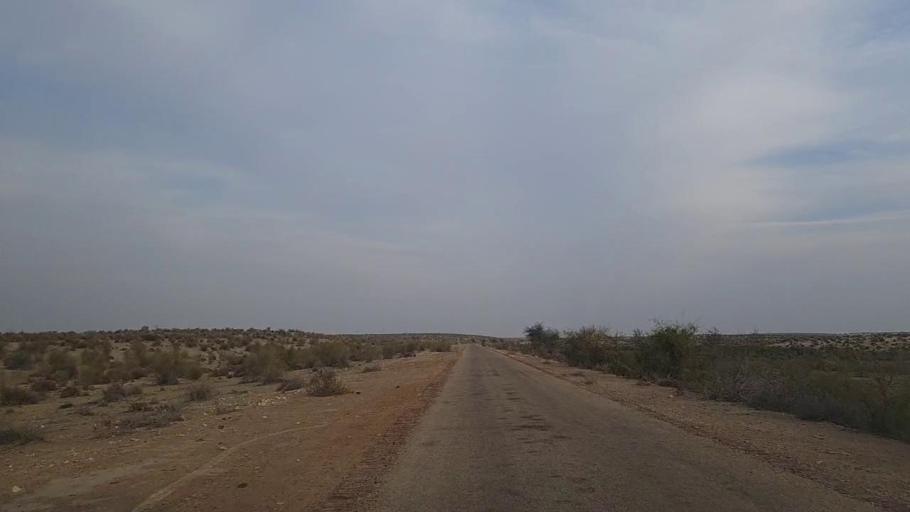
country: PK
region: Sindh
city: Daur
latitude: 26.4938
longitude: 68.5327
